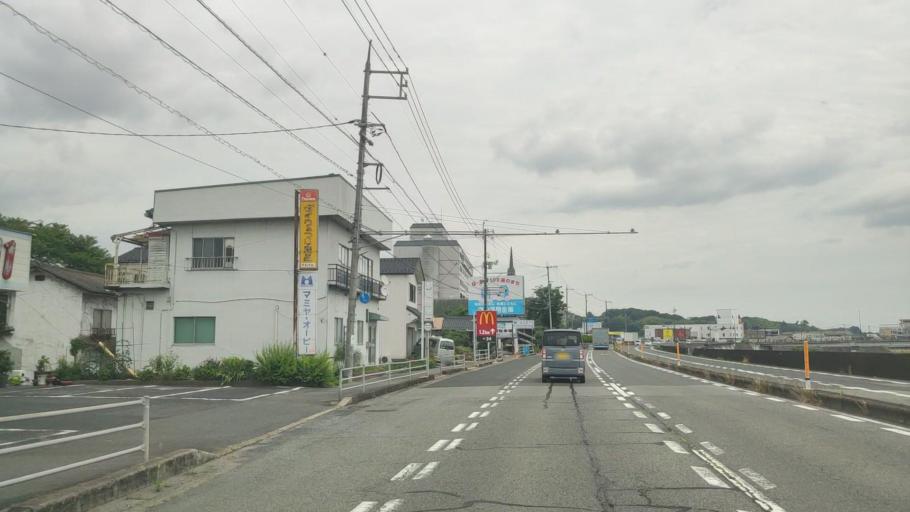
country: JP
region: Okayama
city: Tsuyama
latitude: 35.0628
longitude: 134.0179
